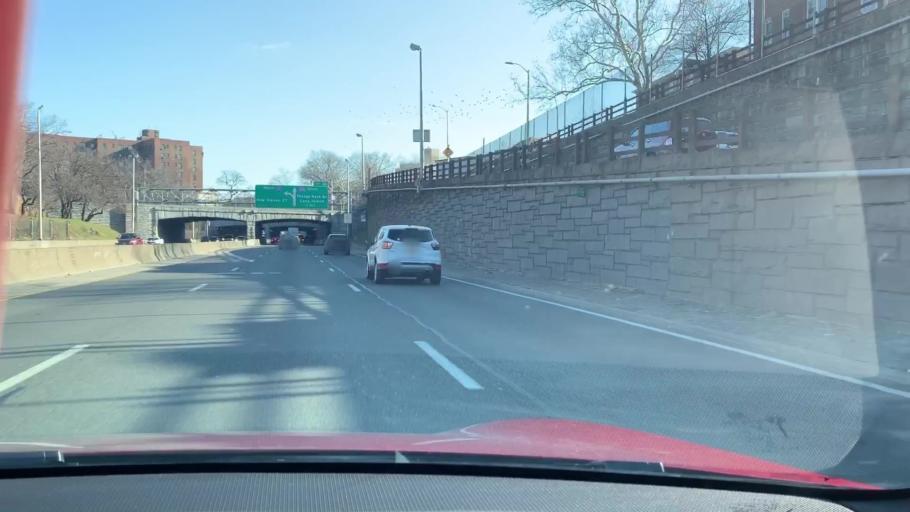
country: US
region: New York
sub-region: Bronx
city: The Bronx
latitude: 40.8344
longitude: -73.8645
